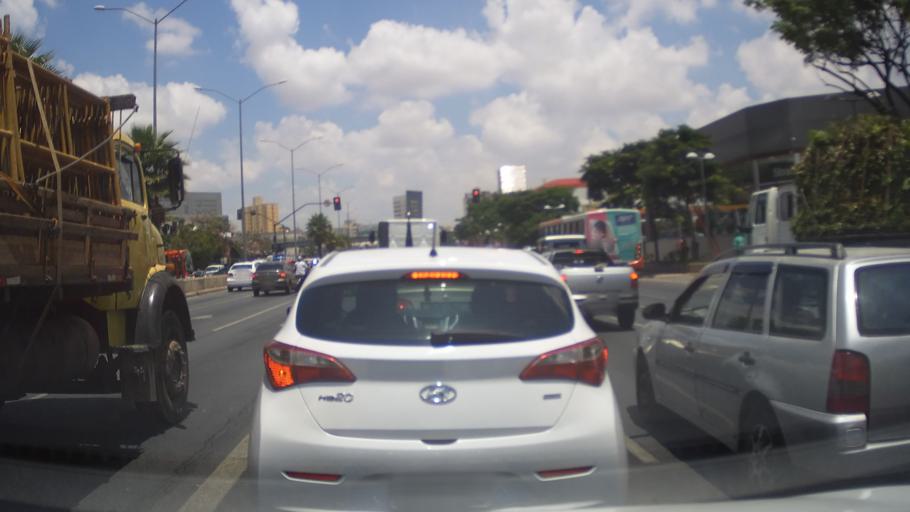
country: BR
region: Minas Gerais
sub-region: Belo Horizonte
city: Belo Horizonte
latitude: -19.9174
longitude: -43.9542
